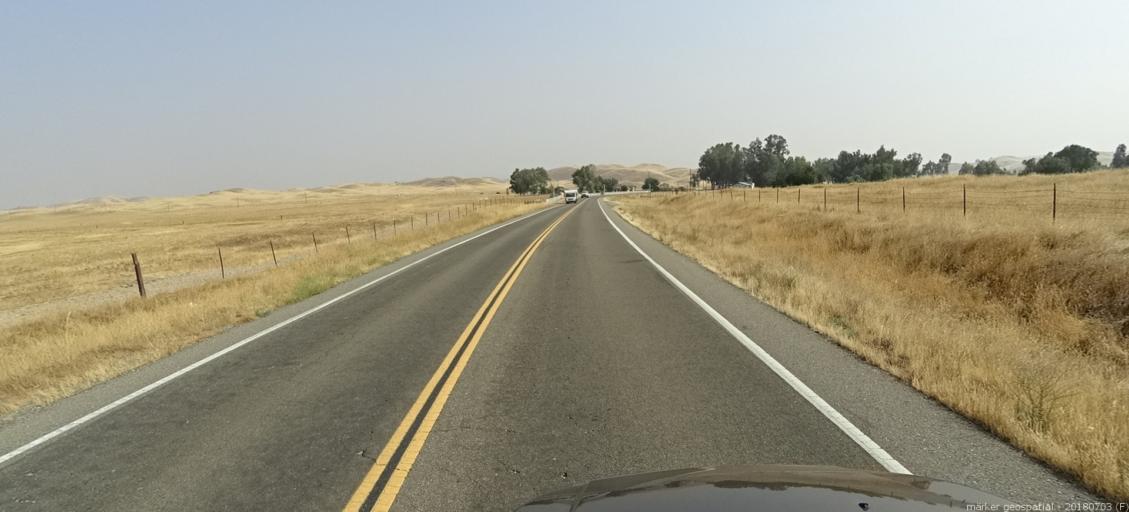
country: US
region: California
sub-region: Madera County
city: Bonadelle Ranchos-Madera Ranchos
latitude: 37.0058
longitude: -119.7366
